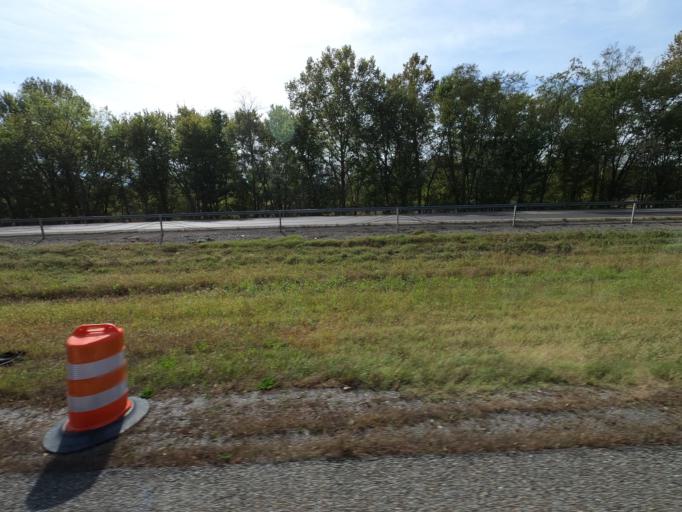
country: US
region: Tennessee
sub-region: Humphreys County
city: New Johnsonville
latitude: 35.8818
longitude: -87.8277
